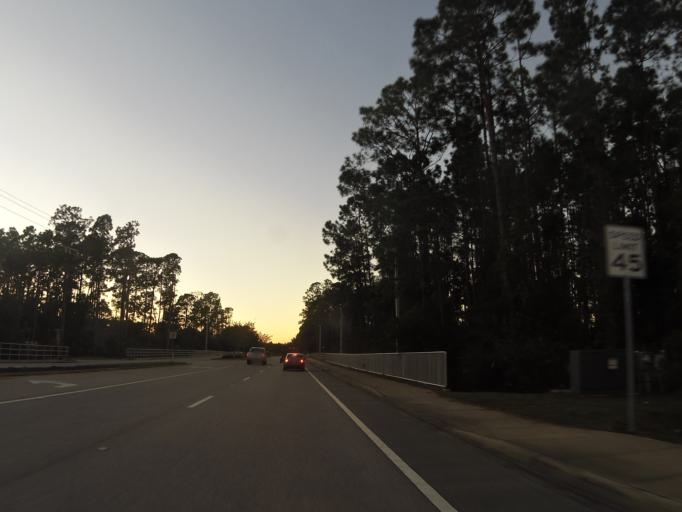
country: US
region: Florida
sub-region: Flagler County
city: Palm Coast
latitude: 29.5656
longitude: -81.2447
